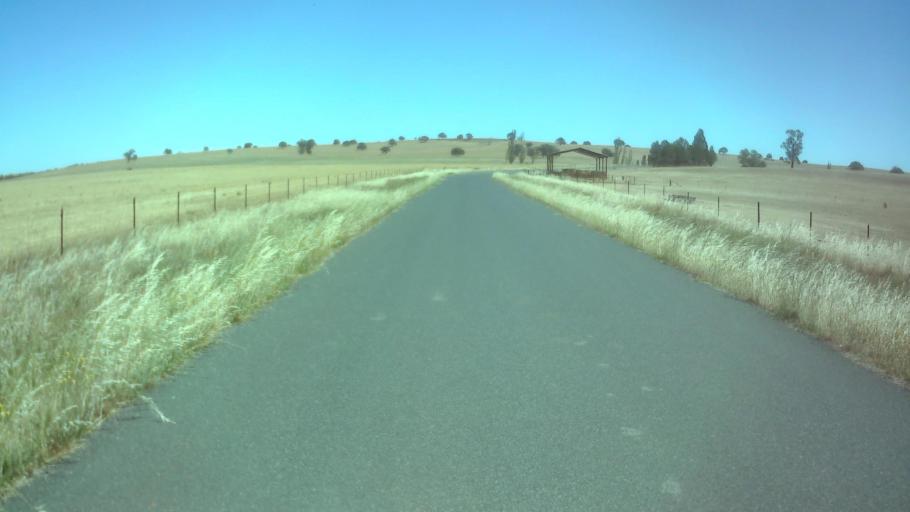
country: AU
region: New South Wales
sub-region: Weddin
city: Grenfell
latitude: -33.9810
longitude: 148.4031
